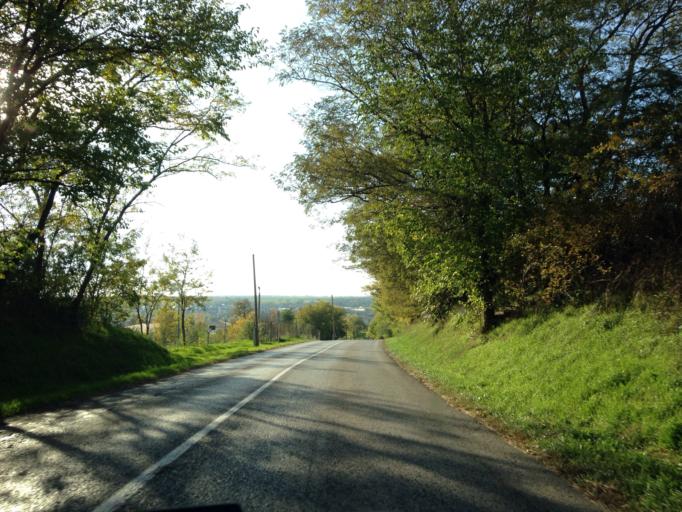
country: SK
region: Nitriansky
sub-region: Okres Komarno
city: Hurbanovo
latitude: 47.8708
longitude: 18.2806
